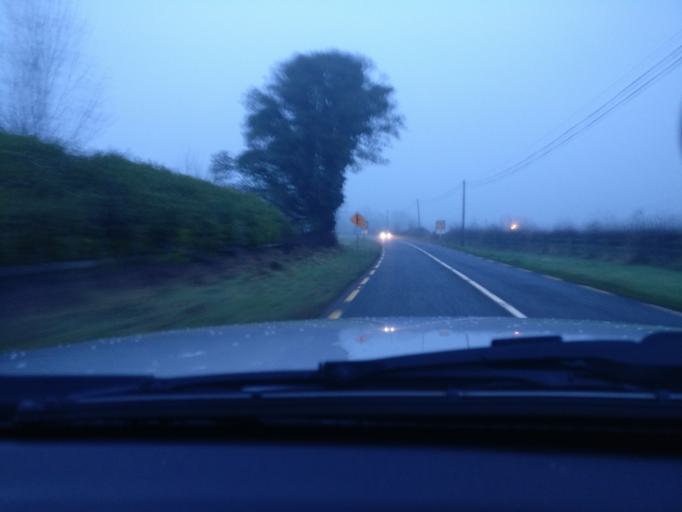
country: IE
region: Leinster
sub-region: An Mhi
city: Athboy
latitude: 53.6089
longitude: -6.9572
